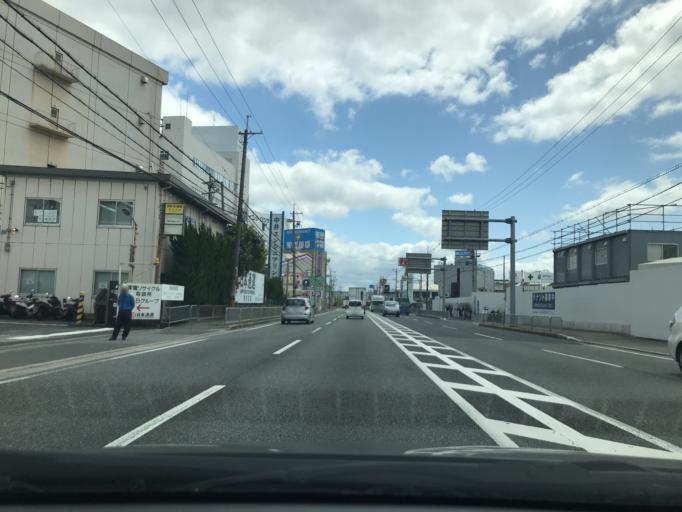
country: JP
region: Osaka
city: Ibaraki
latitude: 34.8347
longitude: 135.5568
